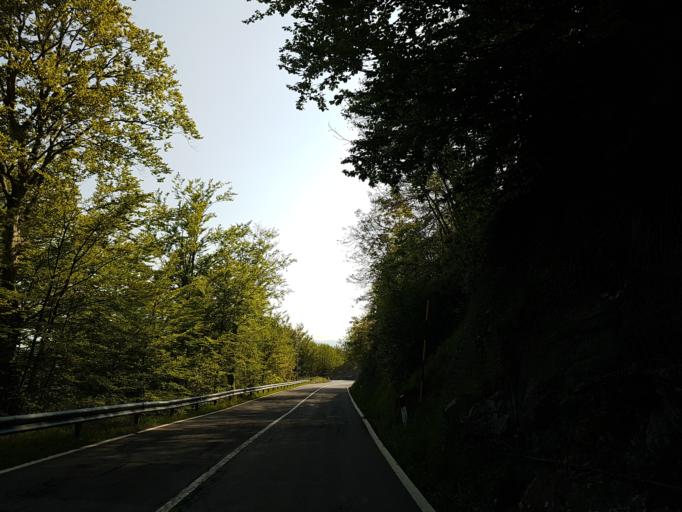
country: IT
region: Emilia-Romagna
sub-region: Forli-Cesena
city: San Piero in Bagno
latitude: 43.7982
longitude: 11.9056
